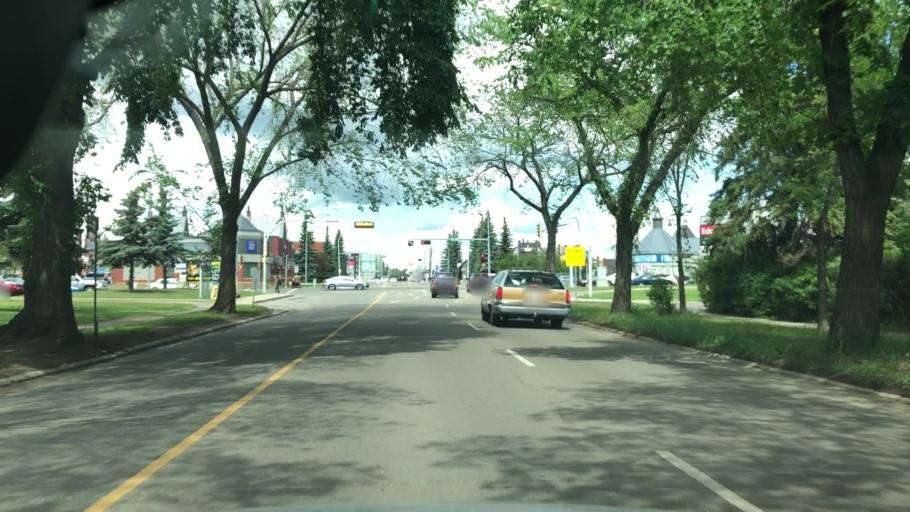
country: CA
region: Alberta
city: Edmonton
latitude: 53.5453
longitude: -113.5214
